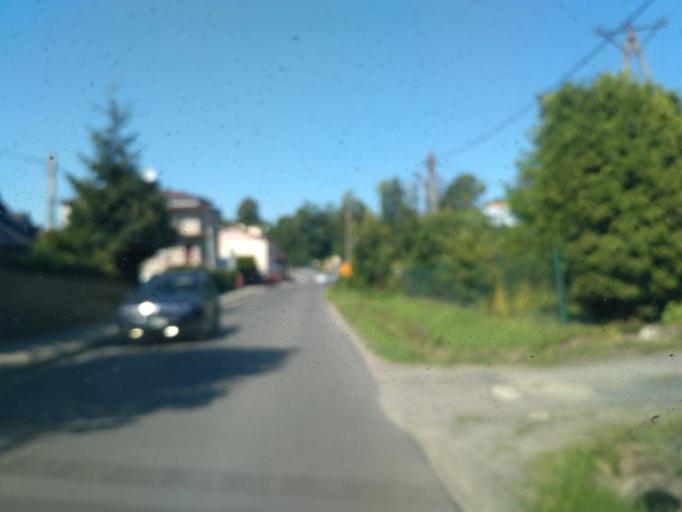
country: PL
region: Subcarpathian Voivodeship
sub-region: Krosno
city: Krosno
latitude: 49.6603
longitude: 21.7520
